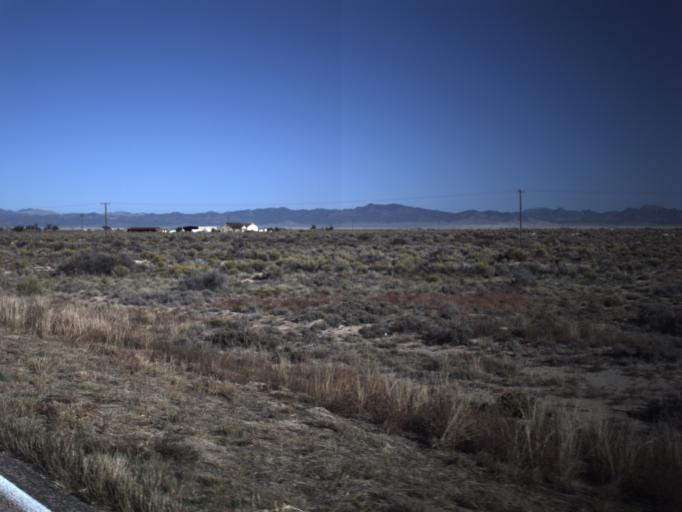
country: US
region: Utah
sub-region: Washington County
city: Enterprise
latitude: 37.7213
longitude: -113.6891
